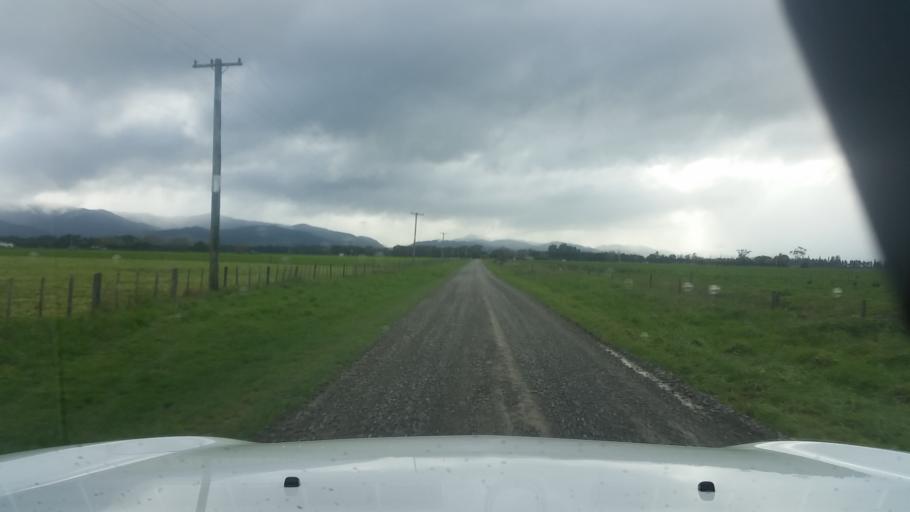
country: NZ
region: Wellington
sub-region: South Wairarapa District
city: Waipawa
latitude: -41.1523
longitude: 175.4197
